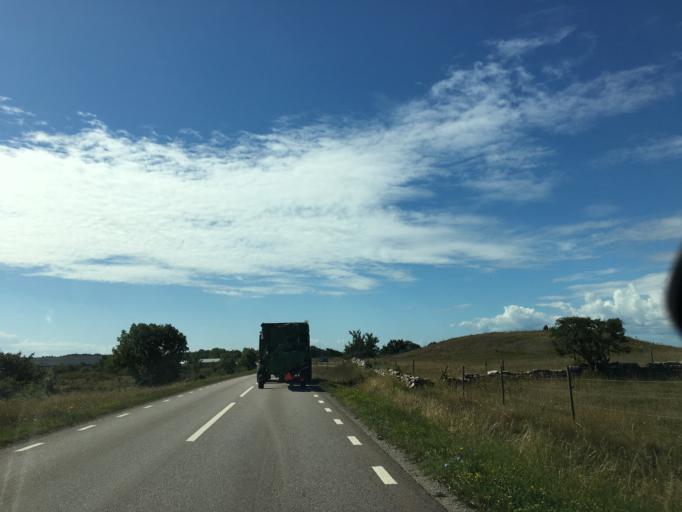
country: SE
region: Kalmar
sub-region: Morbylanga Kommun
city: Moerbylanga
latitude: 56.5290
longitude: 16.4415
